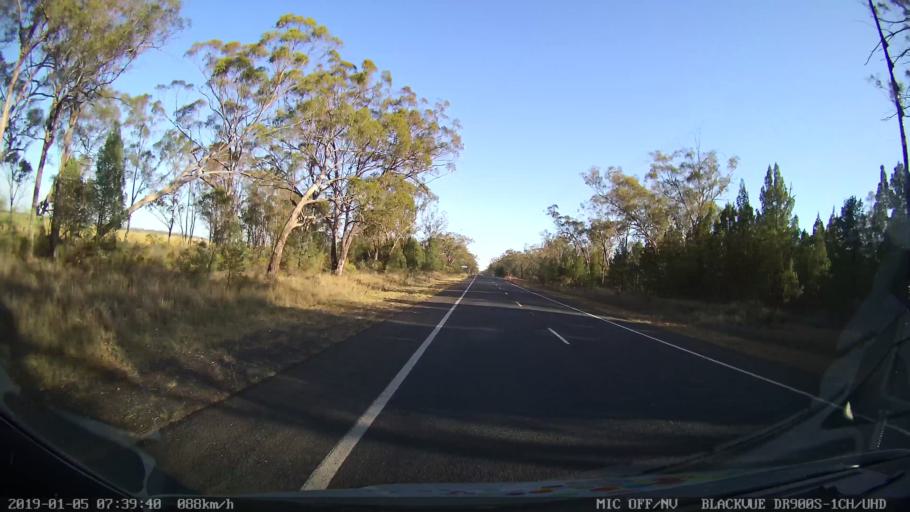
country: AU
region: New South Wales
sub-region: Gilgandra
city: Gilgandra
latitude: -31.9346
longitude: 148.6199
